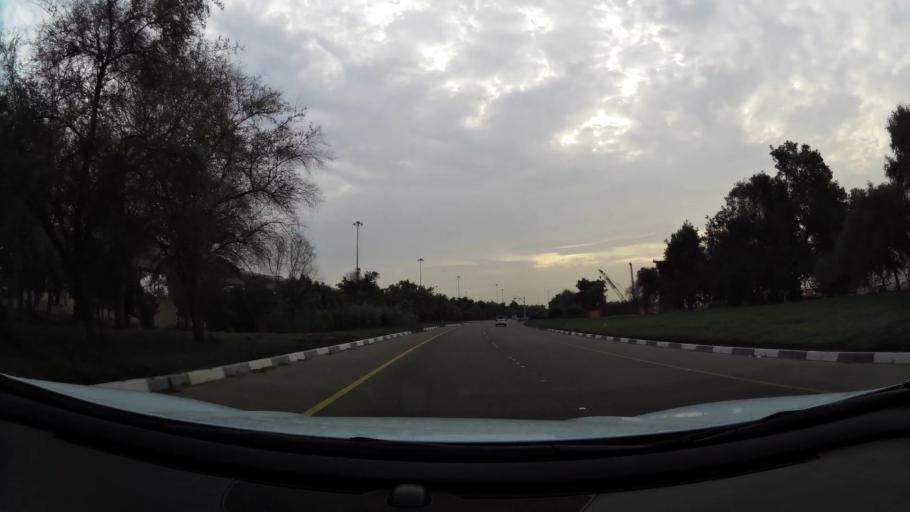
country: AE
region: Abu Dhabi
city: Abu Dhabi
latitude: 24.3894
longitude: 54.5362
